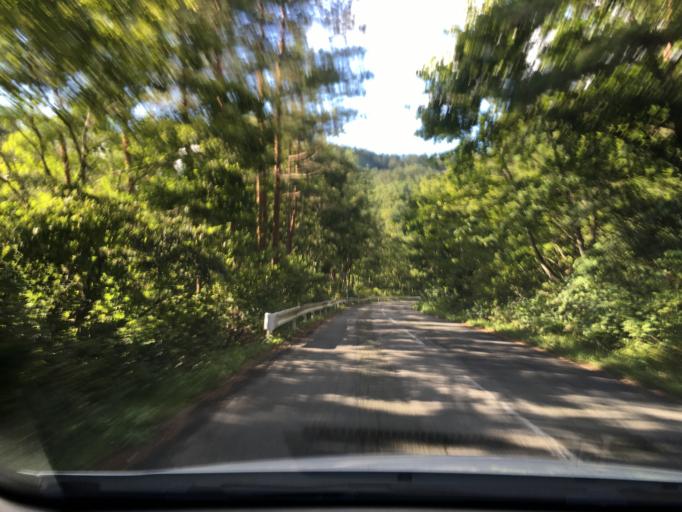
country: JP
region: Yamagata
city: Yonezawa
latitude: 37.9006
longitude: 140.2008
